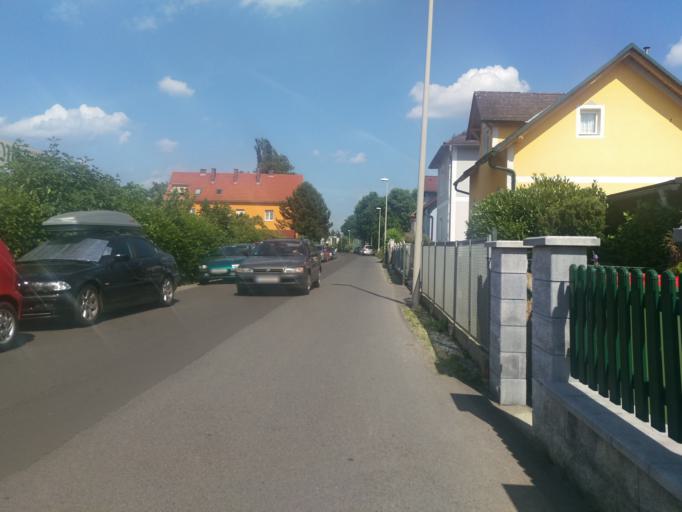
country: AT
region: Styria
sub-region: Politischer Bezirk Graz-Umgebung
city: Feldkirchen bei Graz
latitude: 47.0263
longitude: 15.4253
